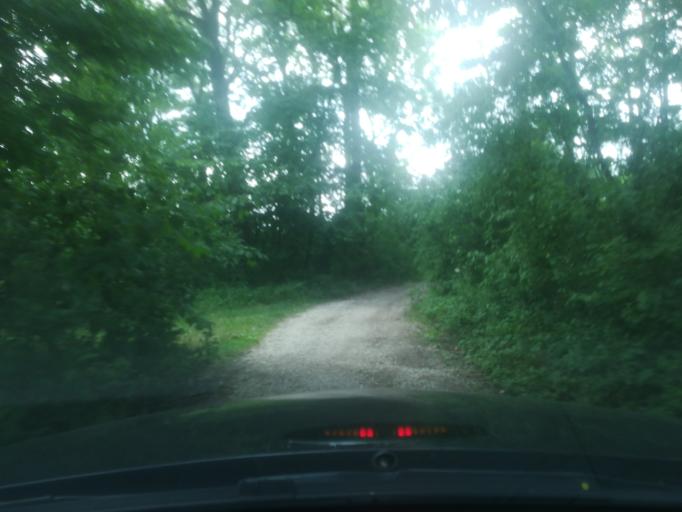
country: AT
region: Upper Austria
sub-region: Wels-Land
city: Marchtrenk
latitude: 48.1814
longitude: 14.1322
